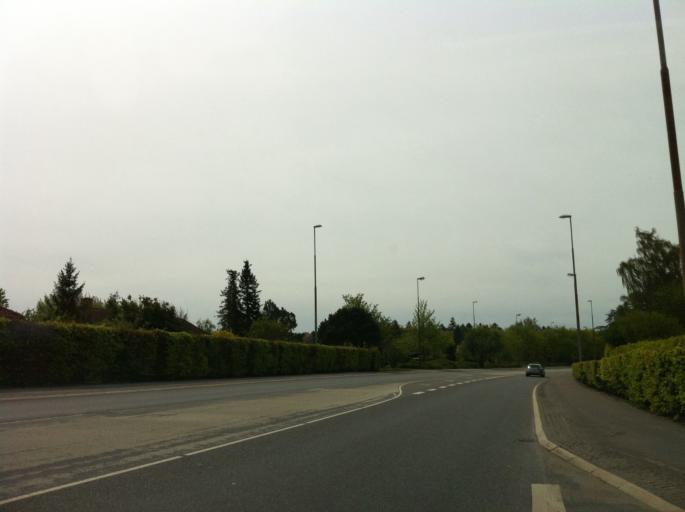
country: DK
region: Zealand
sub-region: Roskilde Kommune
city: Roskilde
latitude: 55.6334
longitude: 12.1061
